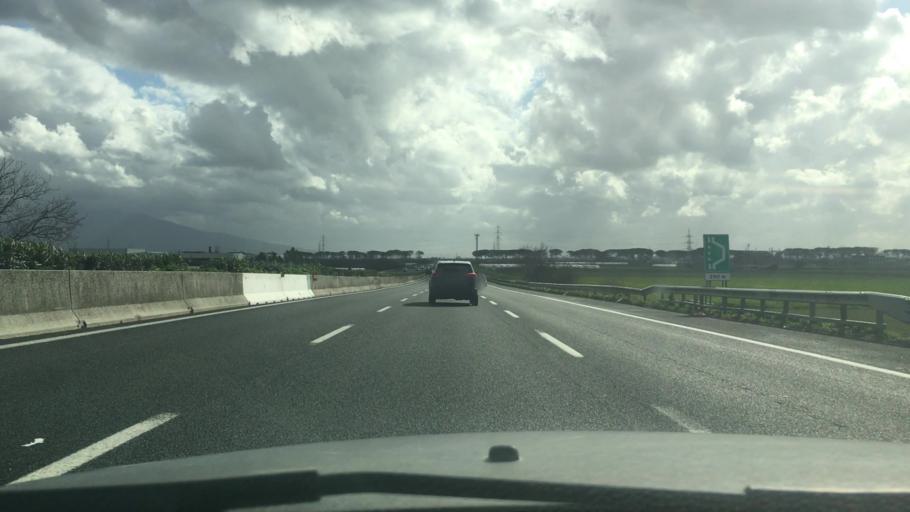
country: IT
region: Campania
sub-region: Provincia di Napoli
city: Pascarola
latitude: 40.9981
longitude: 14.3240
